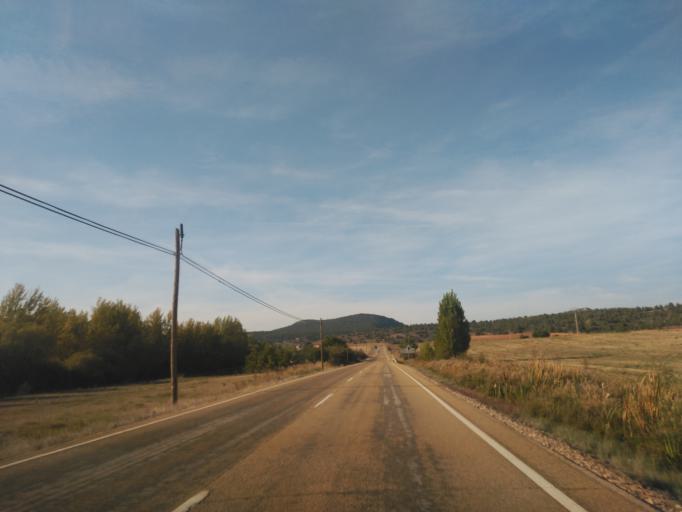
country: ES
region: Castille and Leon
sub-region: Provincia de Soria
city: Ucero
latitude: 41.7045
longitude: -3.0453
